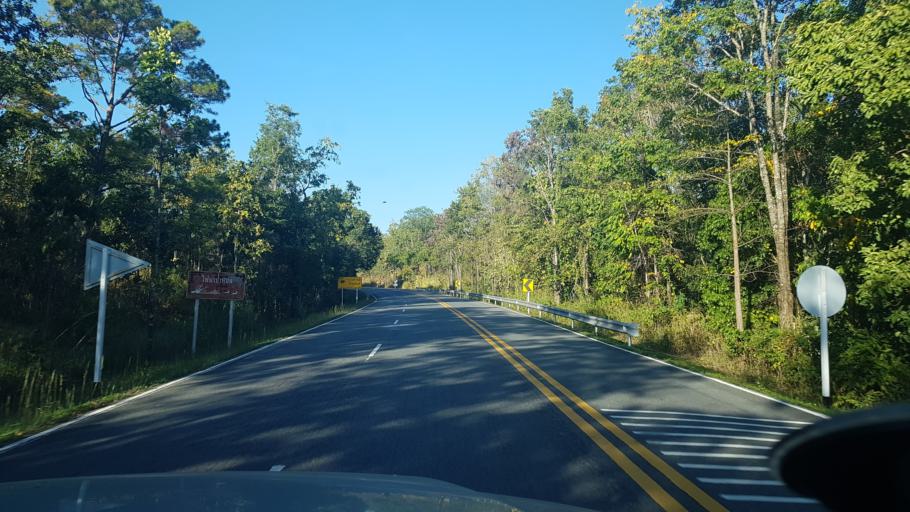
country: TH
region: Phetchabun
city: Nam Nao
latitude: 16.7023
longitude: 101.6476
